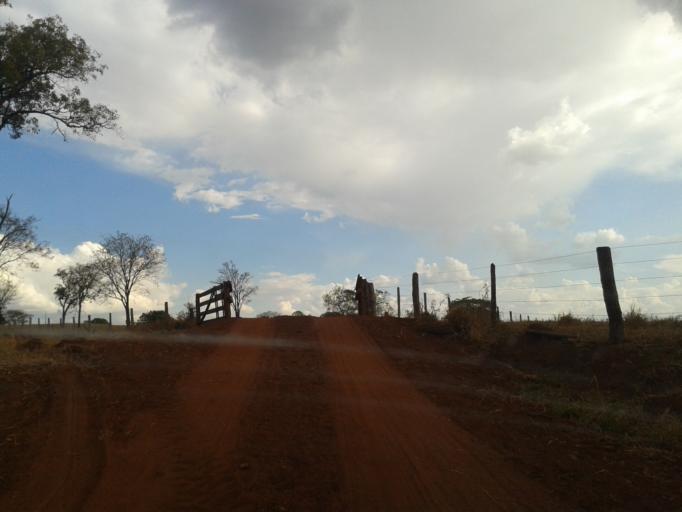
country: BR
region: Minas Gerais
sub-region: Santa Vitoria
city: Santa Vitoria
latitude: -19.1747
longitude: -49.9451
